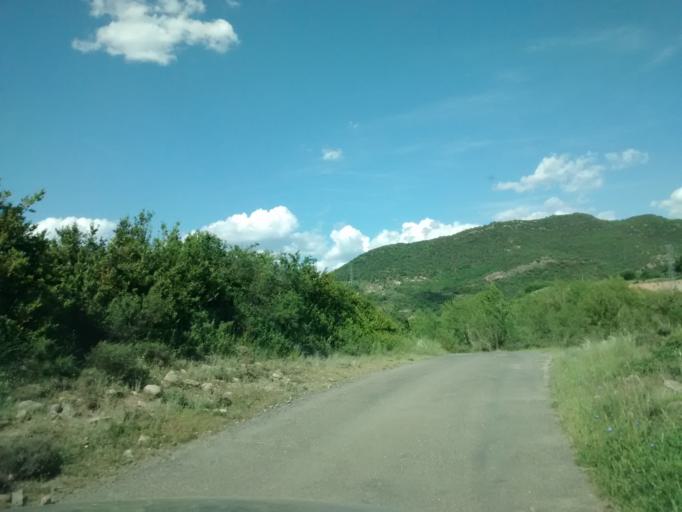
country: ES
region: Aragon
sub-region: Provincia de Huesca
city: Sabinanigo
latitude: 42.4866
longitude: -0.3772
